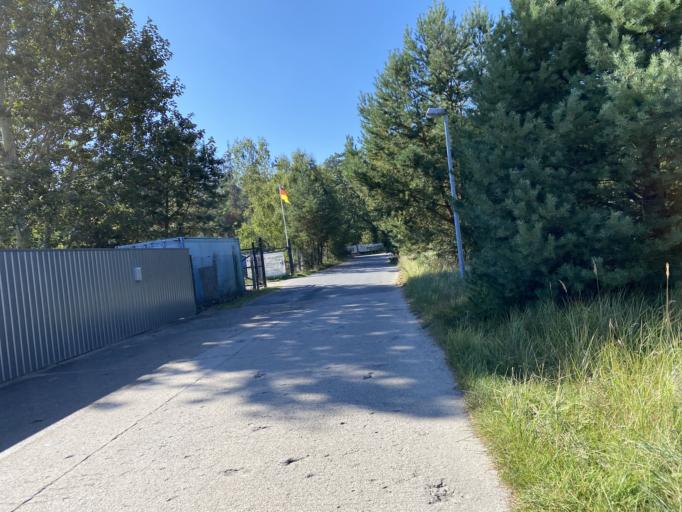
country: DE
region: Mecklenburg-Vorpommern
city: Ostseebad Binz
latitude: 54.4373
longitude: 13.5655
